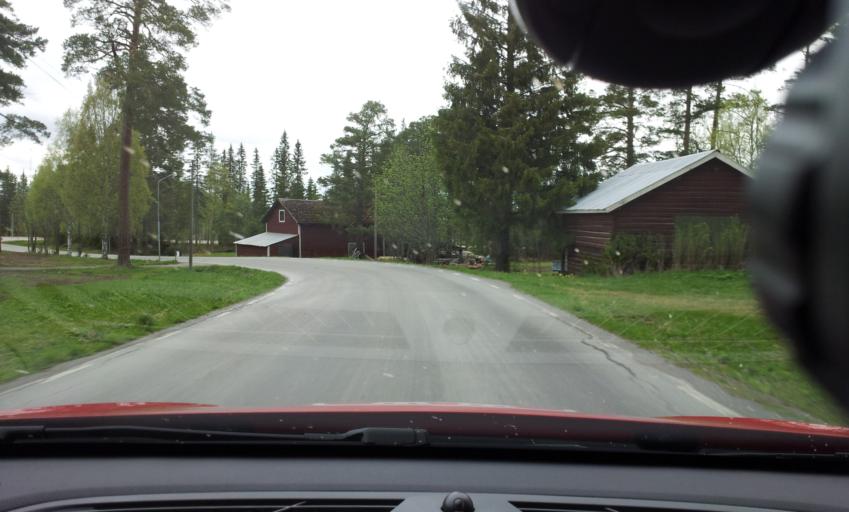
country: SE
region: Jaemtland
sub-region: Bergs Kommun
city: Hoverberg
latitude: 62.7925
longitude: 14.4841
